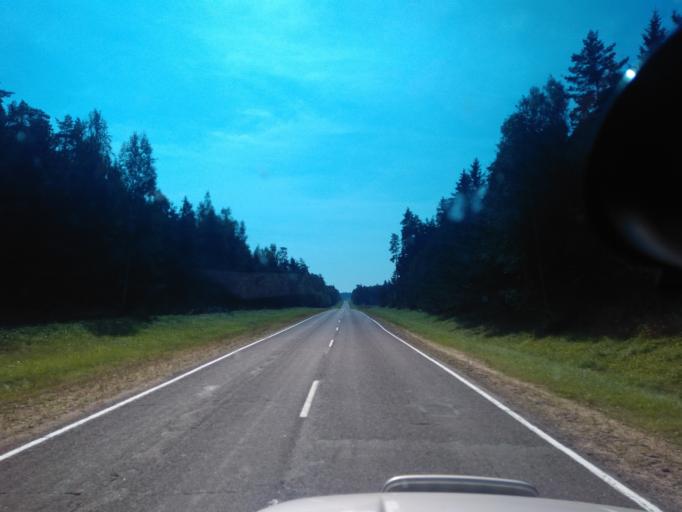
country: BY
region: Minsk
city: Uzda
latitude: 53.3229
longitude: 27.2324
